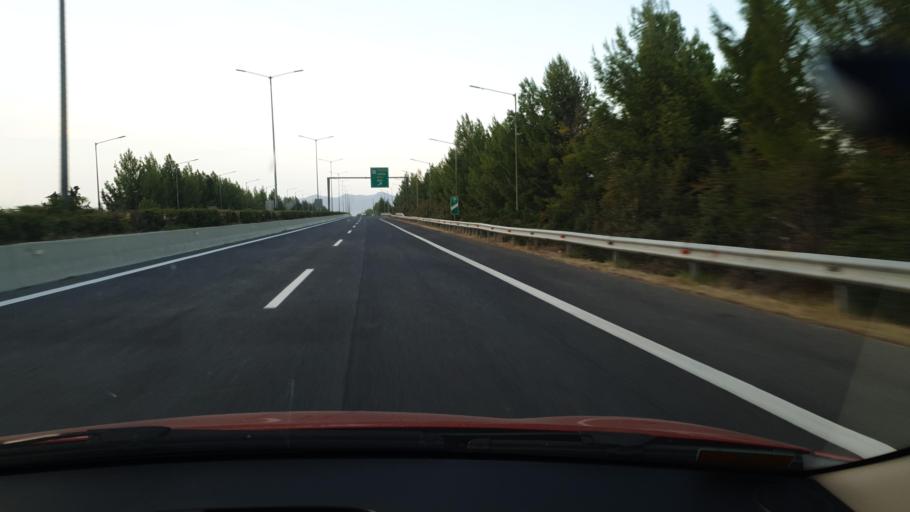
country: GR
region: Thessaly
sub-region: Nomos Larisis
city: Platykampos
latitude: 39.6148
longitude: 22.5027
